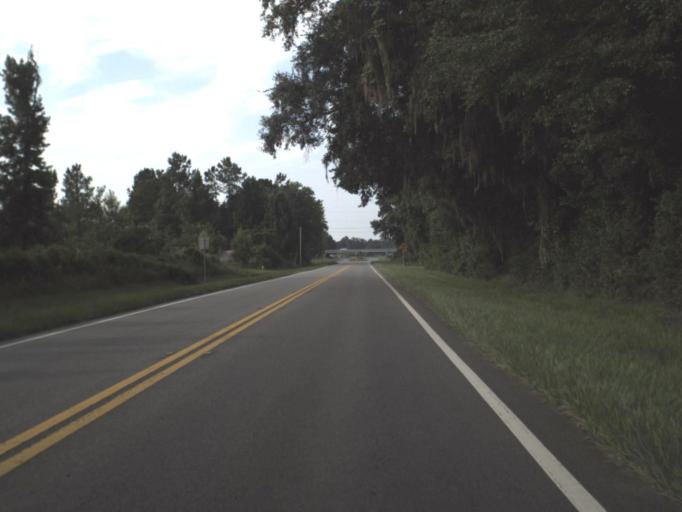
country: US
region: Florida
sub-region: Madison County
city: Madison
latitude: 30.4401
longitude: -83.6268
